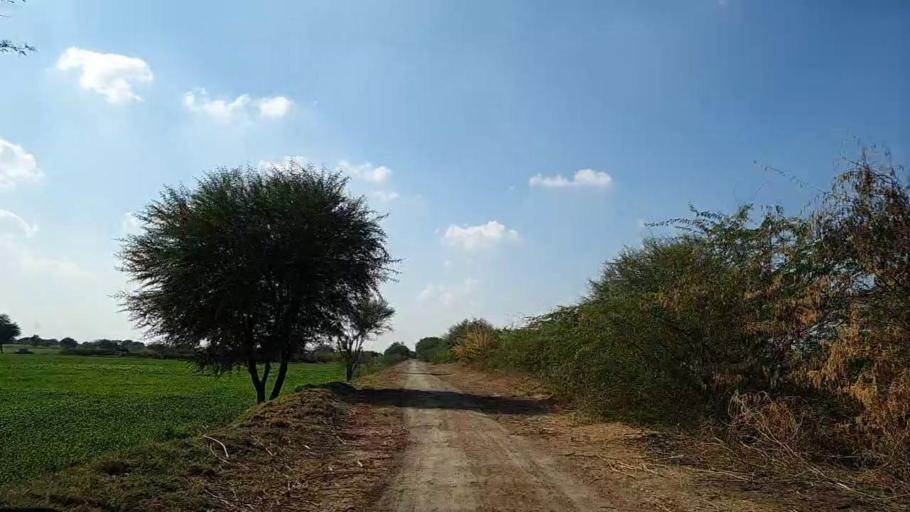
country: PK
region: Sindh
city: Pithoro
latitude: 25.6168
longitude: 69.3868
